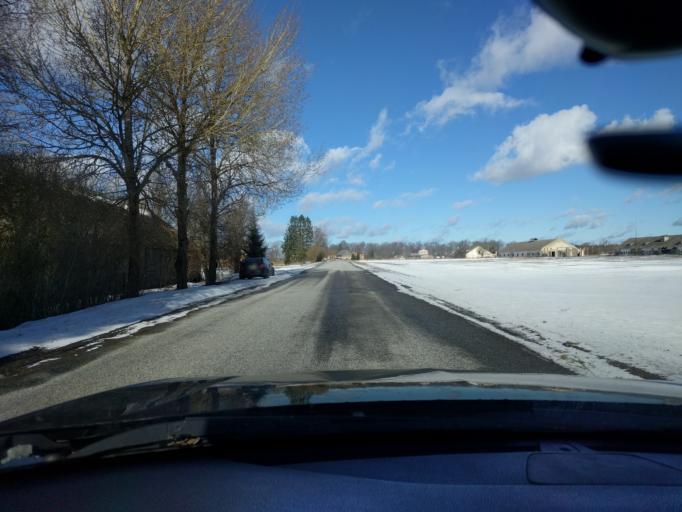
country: EE
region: Harju
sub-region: Raasiku vald
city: Raasiku
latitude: 59.3301
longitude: 25.1583
